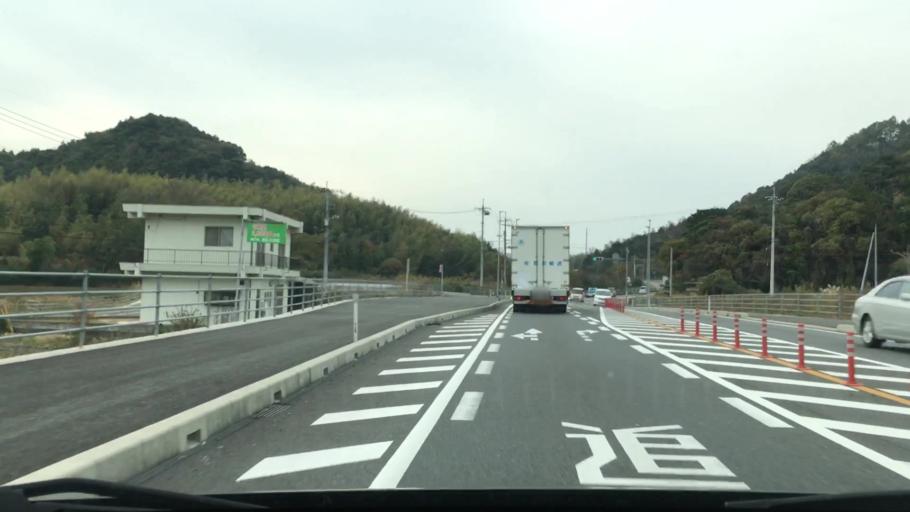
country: JP
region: Yamaguchi
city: Hofu
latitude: 34.0646
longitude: 131.4828
